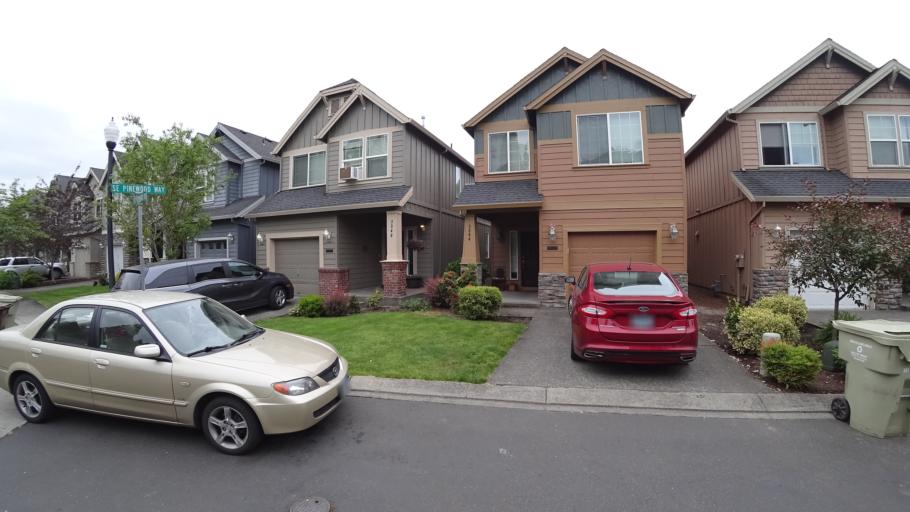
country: US
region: Oregon
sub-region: Washington County
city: Hillsboro
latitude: 45.4944
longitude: -122.9372
